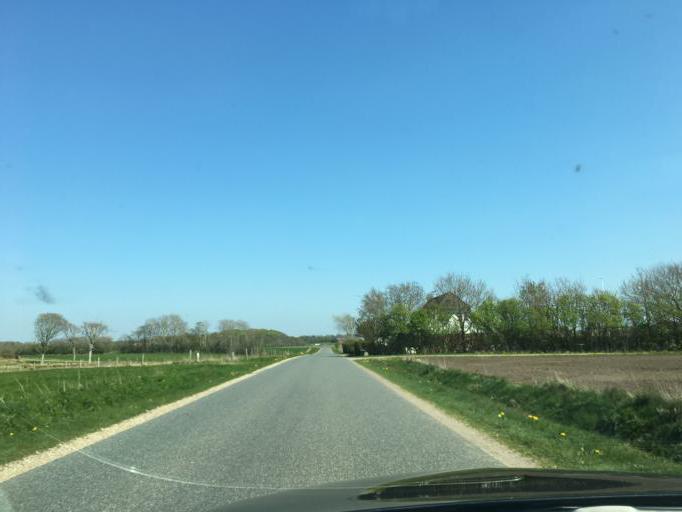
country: DK
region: South Denmark
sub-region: Esbjerg Kommune
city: Bramming
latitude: 55.4978
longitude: 8.6824
